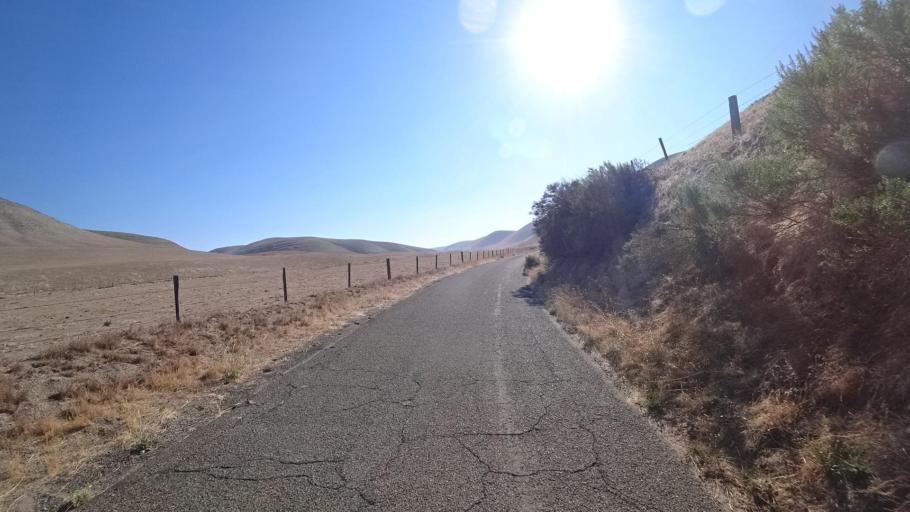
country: US
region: California
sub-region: Monterey County
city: King City
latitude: 36.1938
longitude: -120.9939
